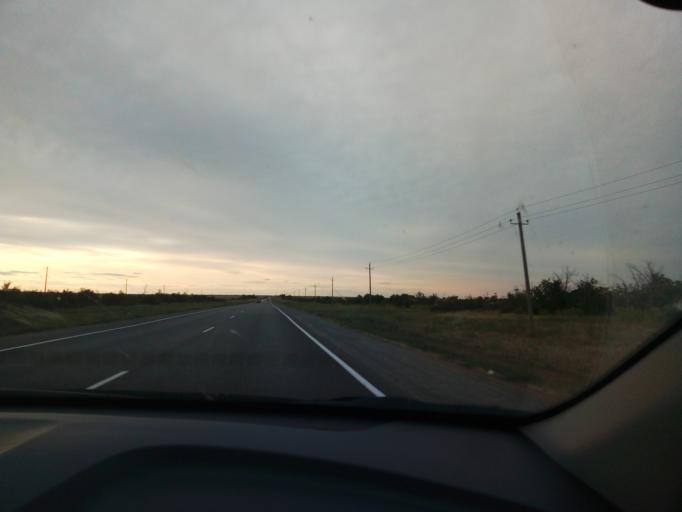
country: RU
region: Volgograd
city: Primorsk
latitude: 49.2409
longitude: 44.8947
